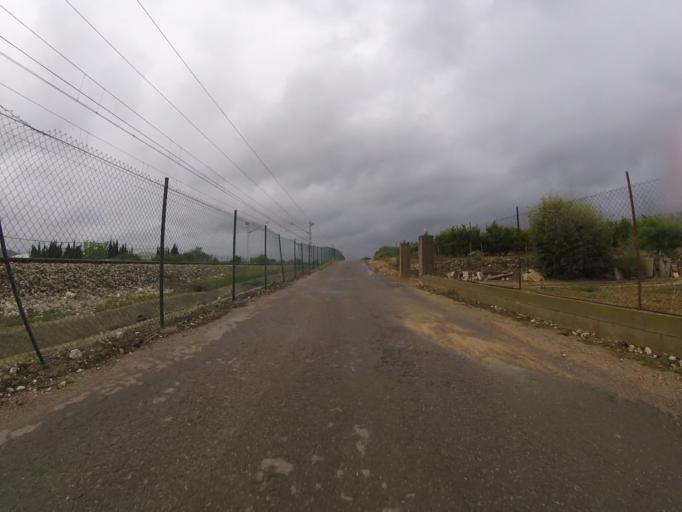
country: ES
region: Valencia
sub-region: Provincia de Castello
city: Alcala de Xivert
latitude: 40.2946
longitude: 0.2244
